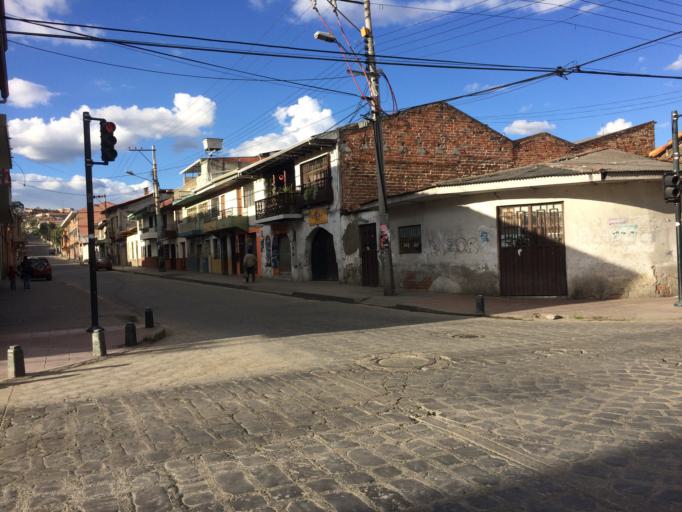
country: EC
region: Azuay
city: Cuenca
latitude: -2.8919
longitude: -79.0069
